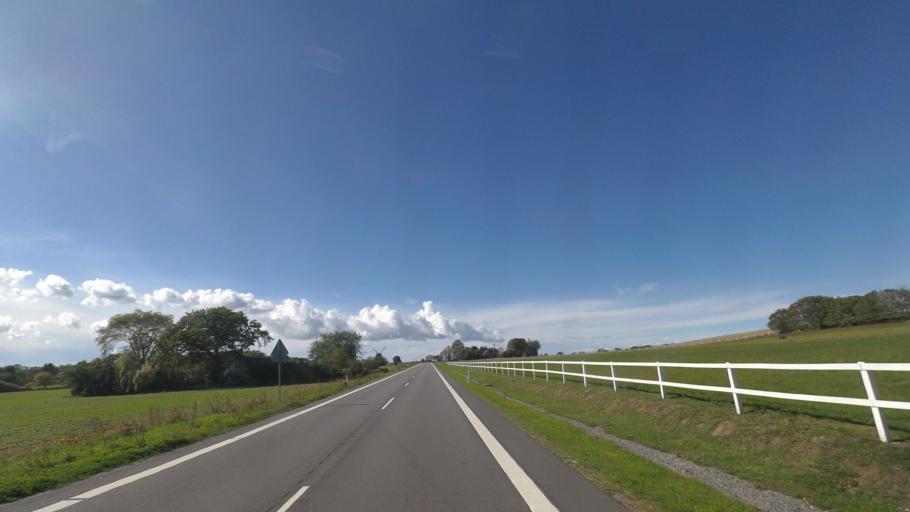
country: DK
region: Capital Region
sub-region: Bornholm Kommune
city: Akirkeby
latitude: 55.0691
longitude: 14.9722
